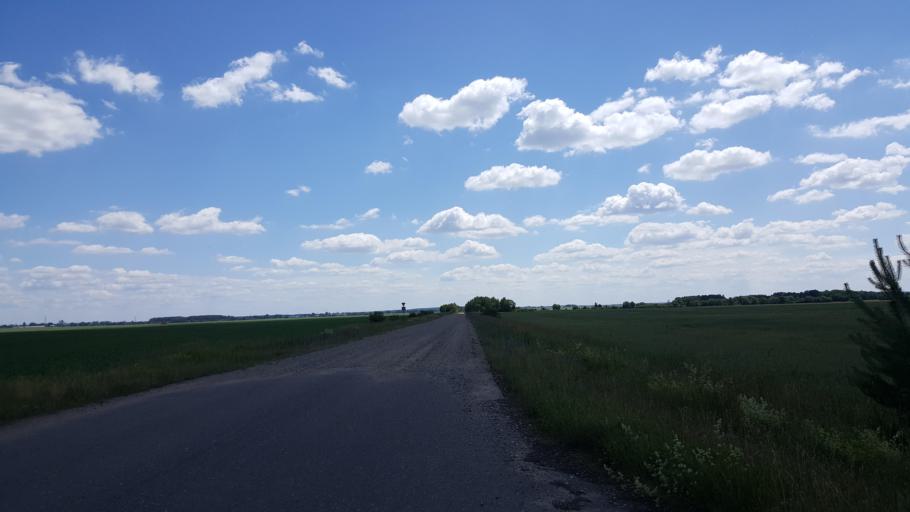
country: PL
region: Podlasie
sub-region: Powiat hajnowski
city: Czeremcha
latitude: 52.5133
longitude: 23.5344
